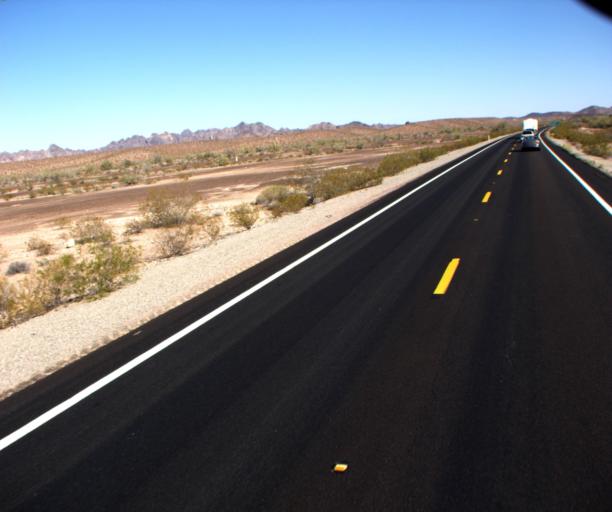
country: US
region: Arizona
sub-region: La Paz County
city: Quartzsite
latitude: 33.1823
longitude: -114.2754
